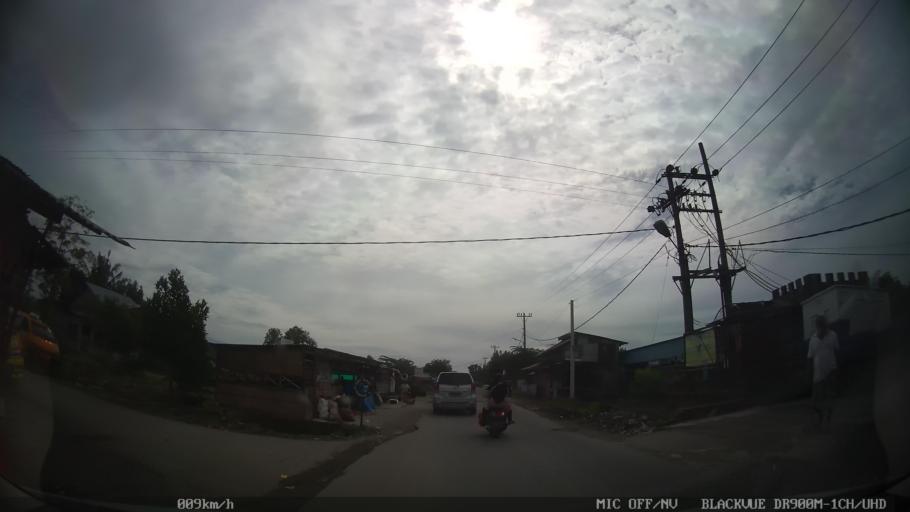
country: ID
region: North Sumatra
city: Medan
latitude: 3.6202
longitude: 98.7538
